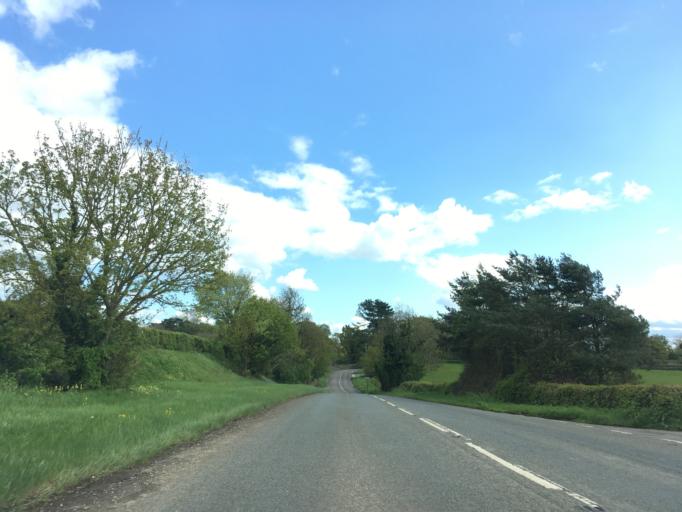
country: GB
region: England
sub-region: South Gloucestershire
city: Wickwar
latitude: 51.5989
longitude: -2.4057
